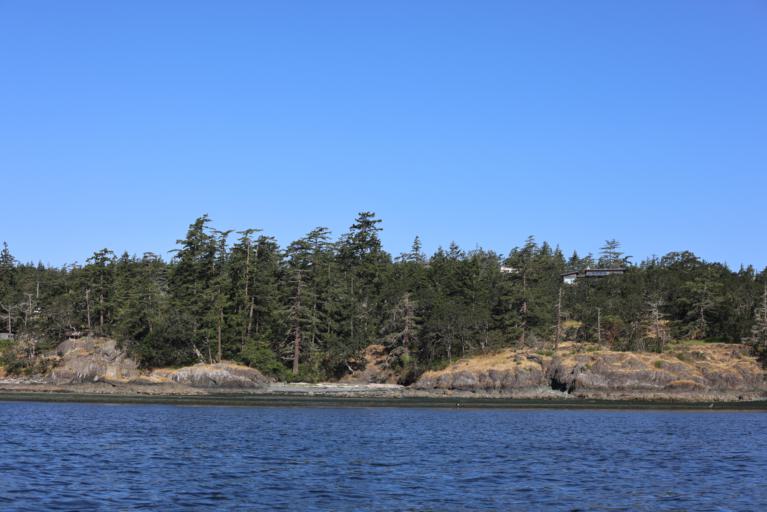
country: CA
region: British Columbia
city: Metchosin
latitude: 48.3552
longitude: -123.5404
